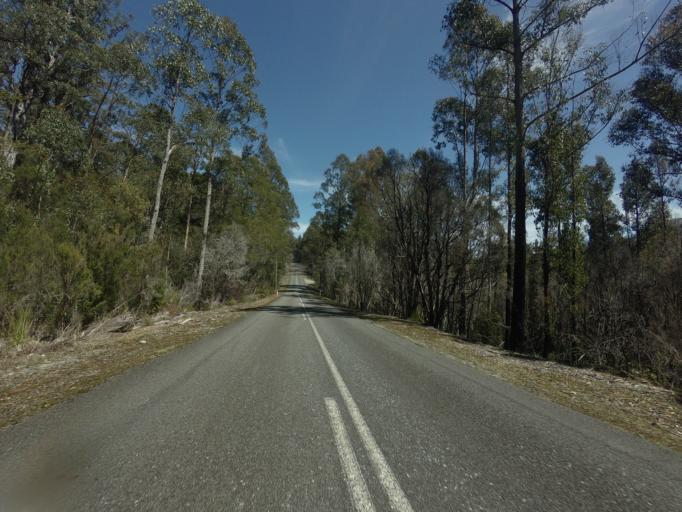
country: AU
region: Tasmania
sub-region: Huon Valley
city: Geeveston
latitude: -42.8397
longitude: 146.2578
